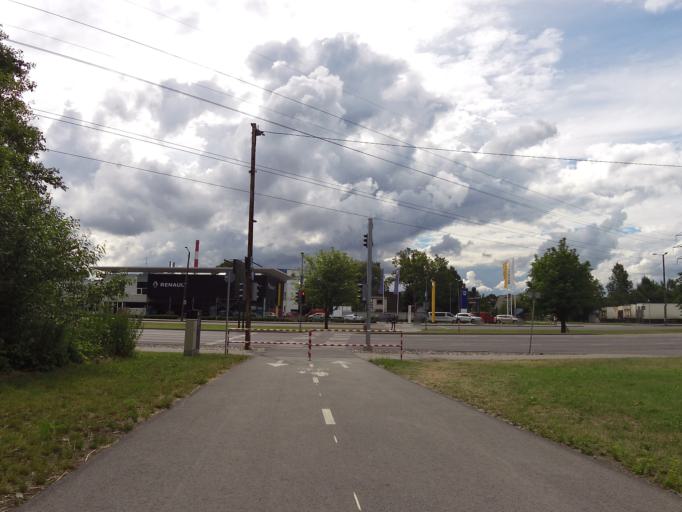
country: EE
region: Harju
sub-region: Tallinna linn
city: Tallinn
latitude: 59.4298
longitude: 24.6848
